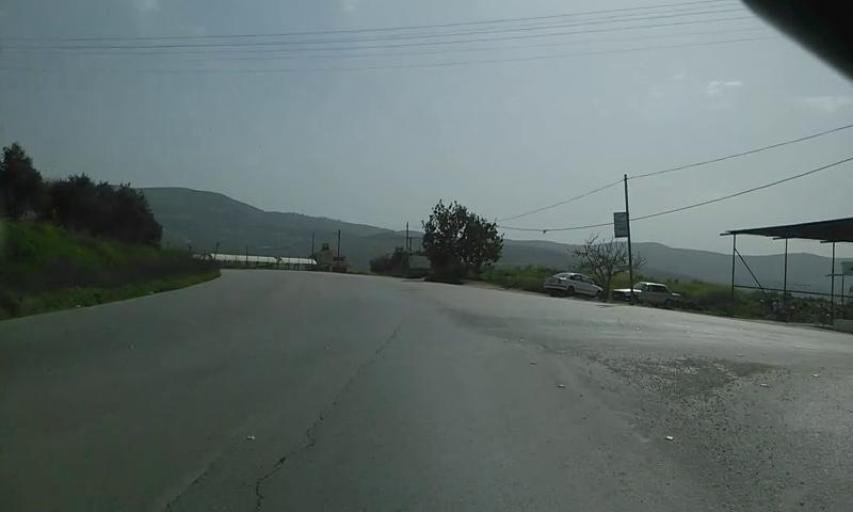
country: PS
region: West Bank
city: `Ajjah
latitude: 32.3475
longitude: 35.2010
